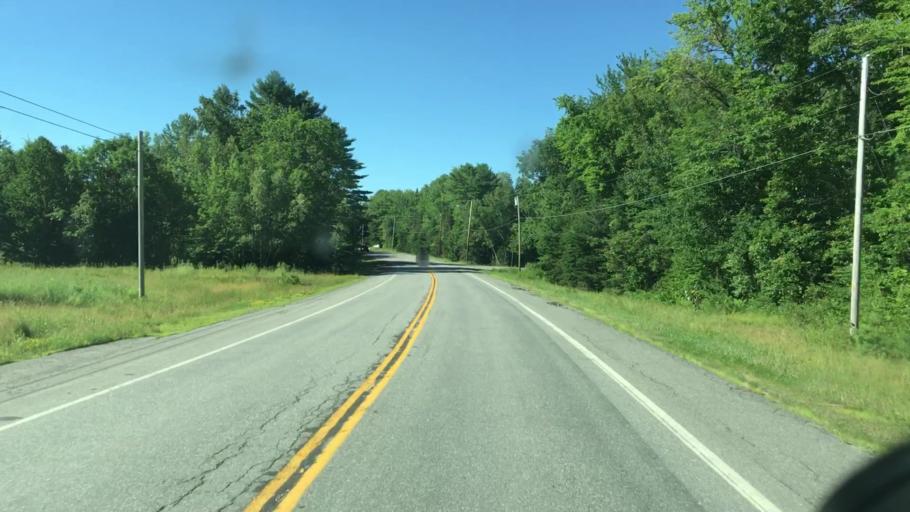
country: US
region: Maine
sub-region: Penobscot County
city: Howland
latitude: 45.2718
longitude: -68.6380
